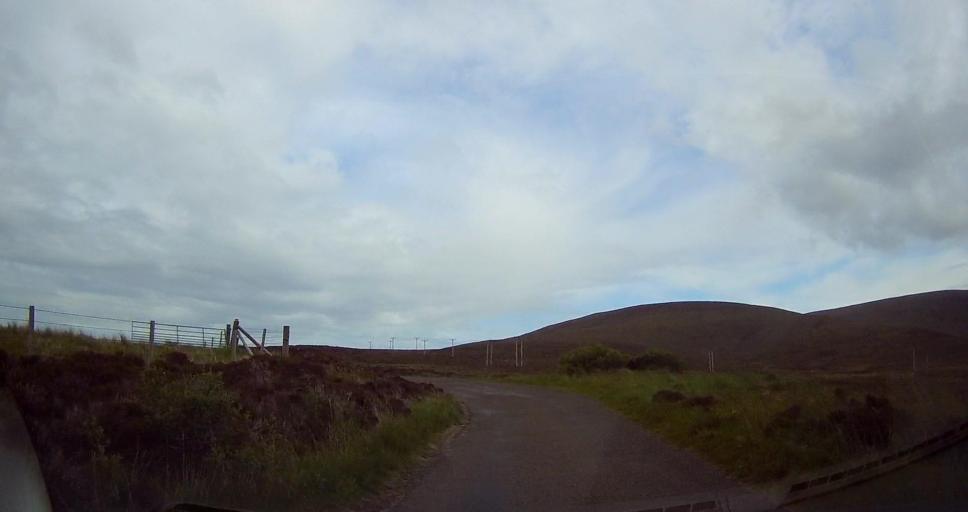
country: GB
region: Scotland
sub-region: Orkney Islands
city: Stromness
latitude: 58.9031
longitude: -3.3053
